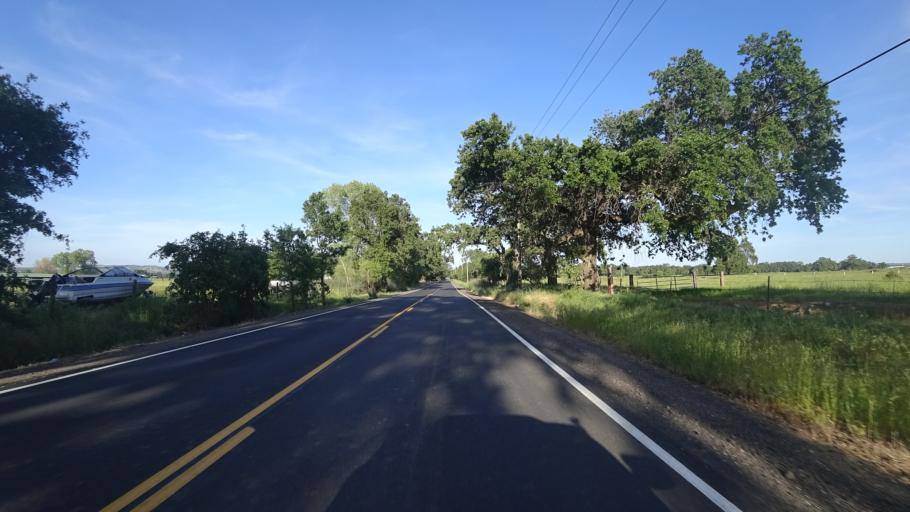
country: US
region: California
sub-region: Placer County
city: Lincoln
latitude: 38.9265
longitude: -121.2868
